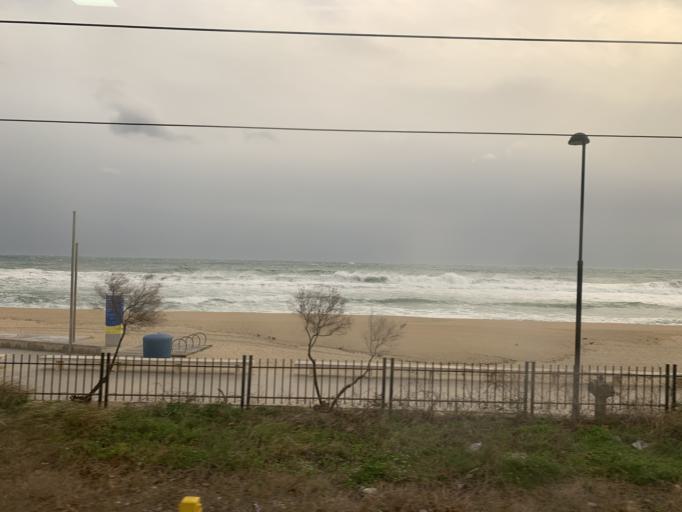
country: ES
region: Catalonia
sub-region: Provincia de Barcelona
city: Montgat
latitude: 41.4597
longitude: 2.2667
